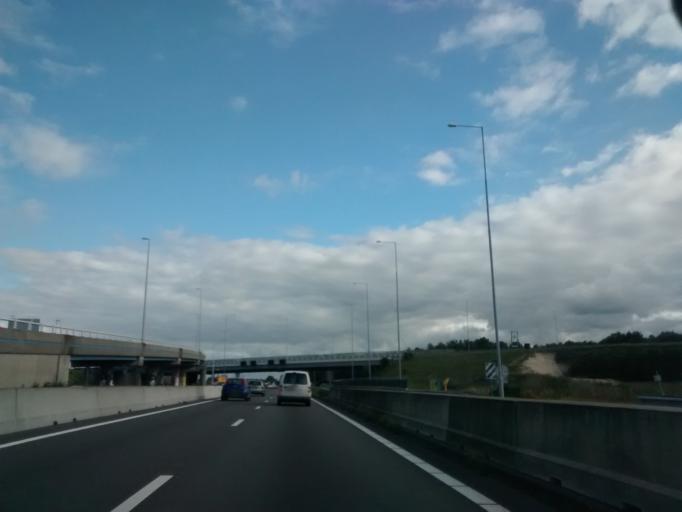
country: NL
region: North Holland
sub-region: Gemeente Weesp
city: Weesp
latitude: 52.3155
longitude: 5.1029
